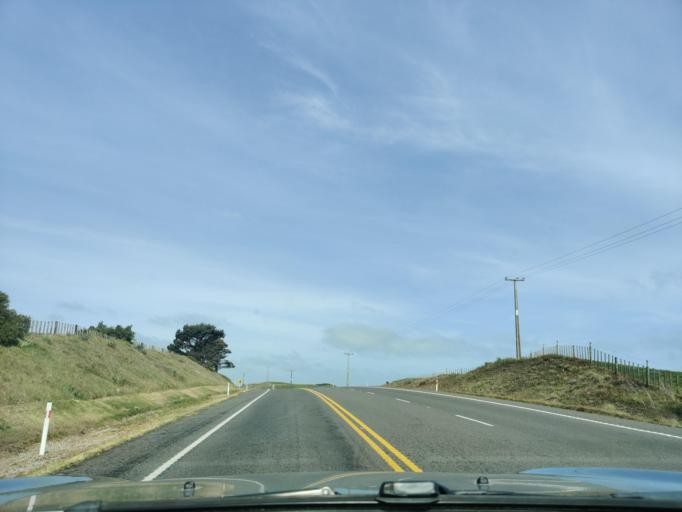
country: NZ
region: Taranaki
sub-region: South Taranaki District
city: Patea
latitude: -39.7352
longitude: 174.4527
